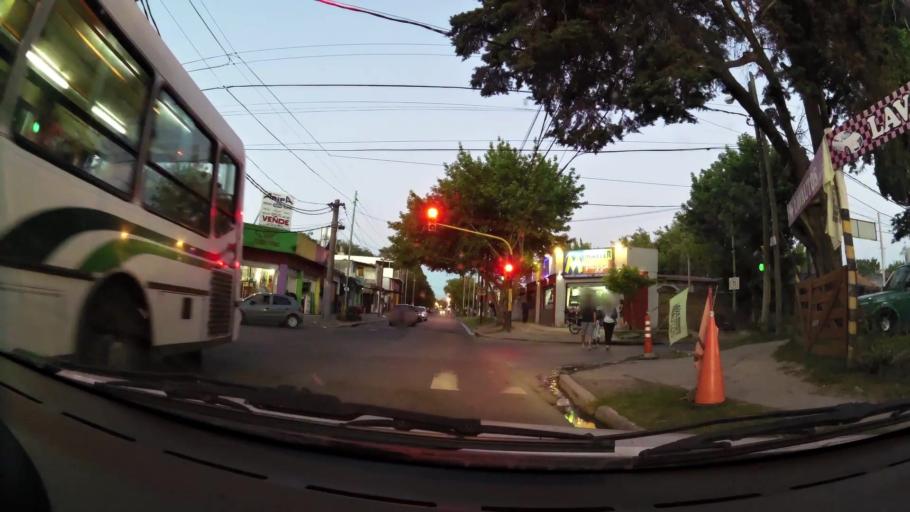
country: AR
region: Buenos Aires
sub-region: Partido de Quilmes
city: Quilmes
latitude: -34.7979
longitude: -58.1718
